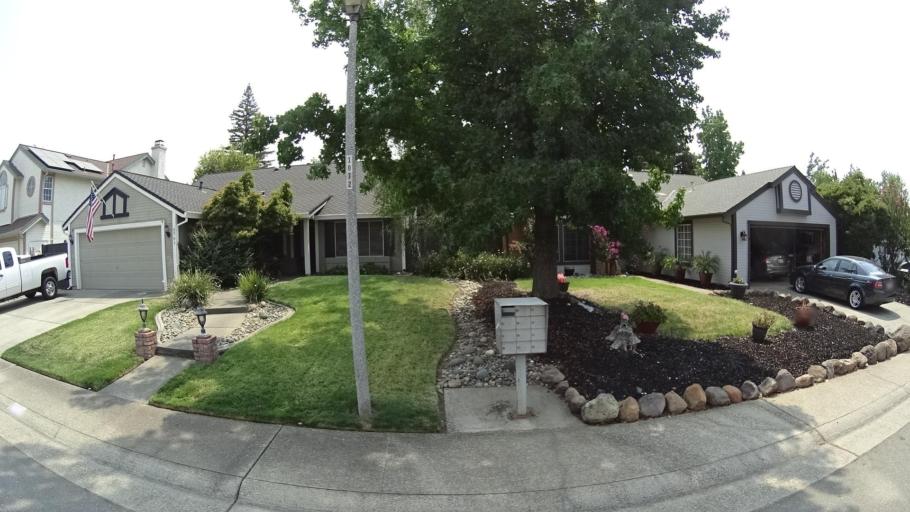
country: US
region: California
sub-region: Placer County
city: Rocklin
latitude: 38.8009
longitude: -121.2609
